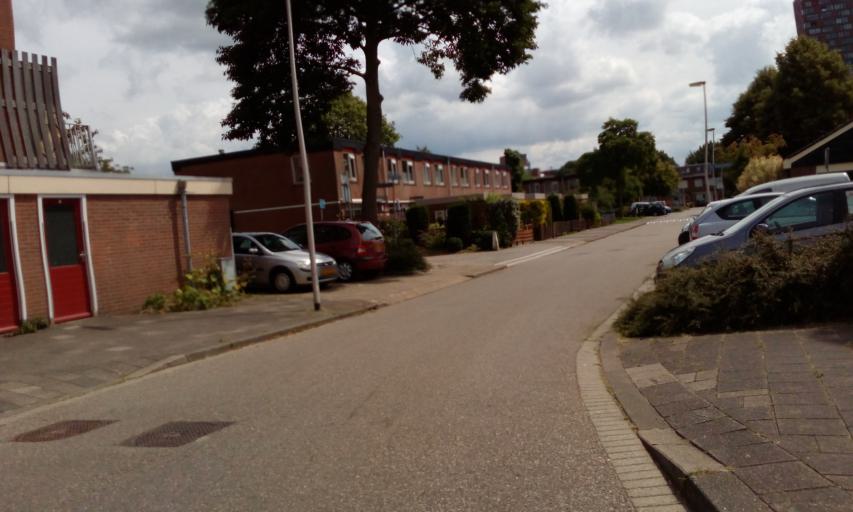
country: NL
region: South Holland
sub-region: Gemeente Zoetermeer
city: Zoetermeer
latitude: 52.0631
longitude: 4.4800
